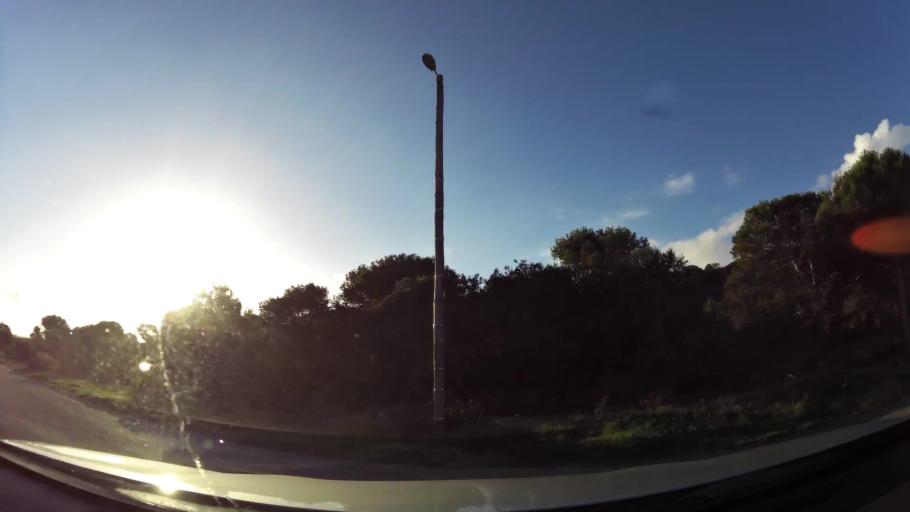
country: ZA
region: Western Cape
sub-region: Eden District Municipality
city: George
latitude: -34.0020
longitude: 22.6569
